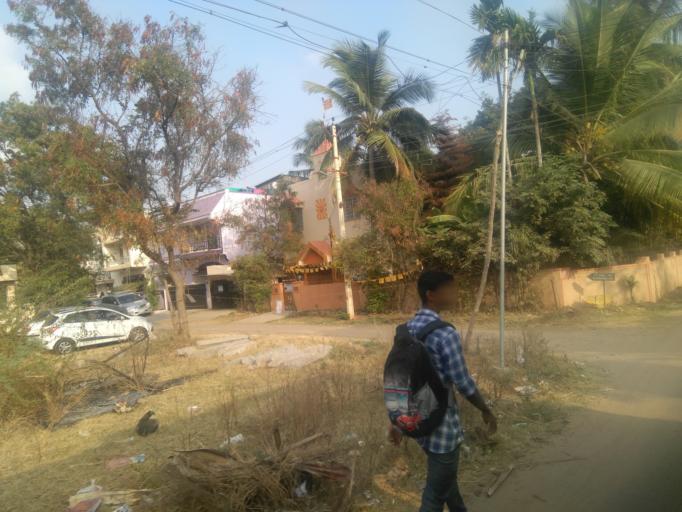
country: IN
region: Tamil Nadu
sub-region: Coimbatore
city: Perur
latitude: 11.0313
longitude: 76.8912
